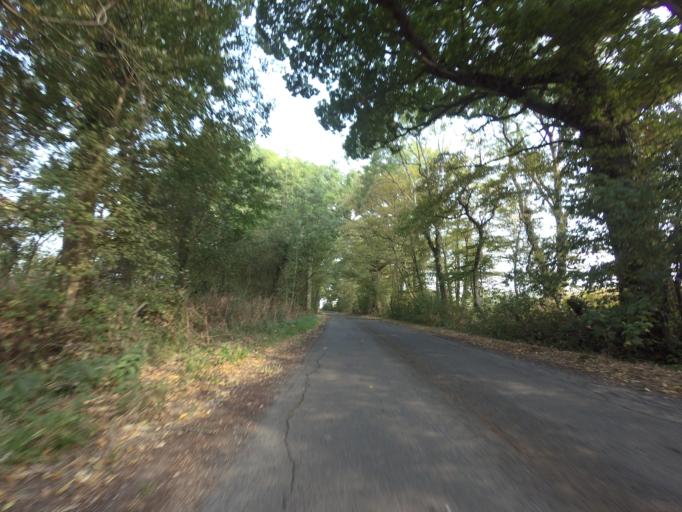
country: GB
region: England
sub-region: Kent
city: Tenterden
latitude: 51.1231
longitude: 0.6749
